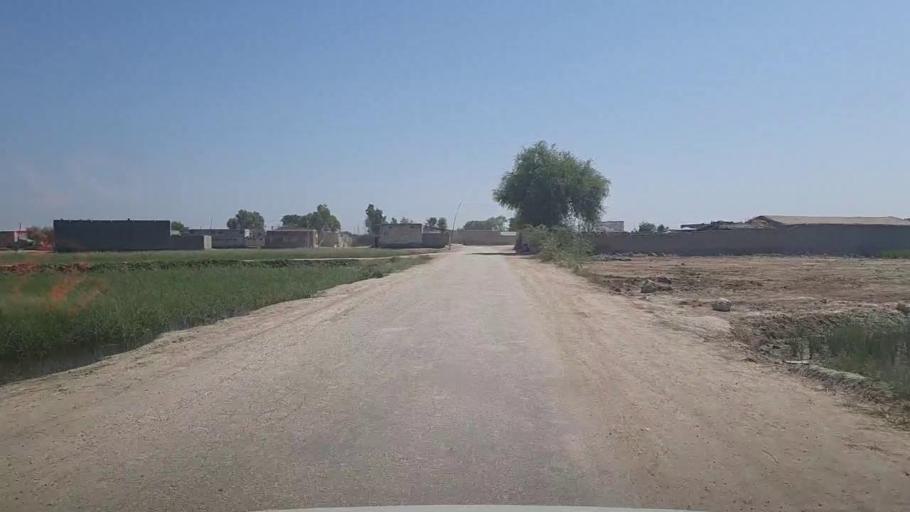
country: PK
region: Sindh
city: Kashmor
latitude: 28.2894
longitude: 69.4357
